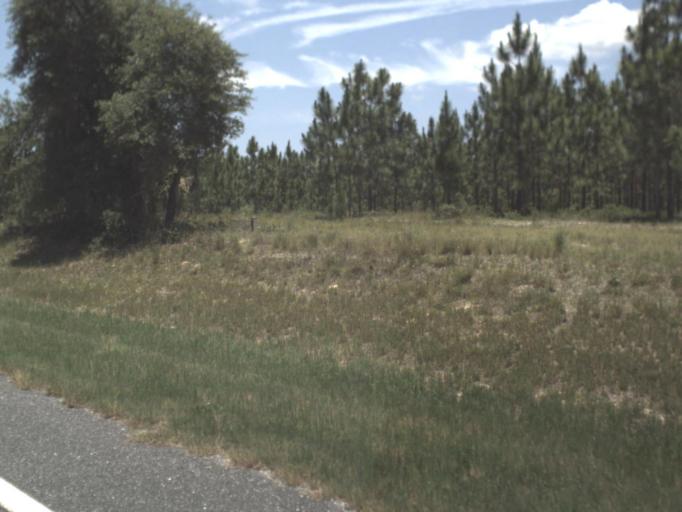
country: US
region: Florida
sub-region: Levy County
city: Williston Highlands
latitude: 29.2228
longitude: -82.5652
